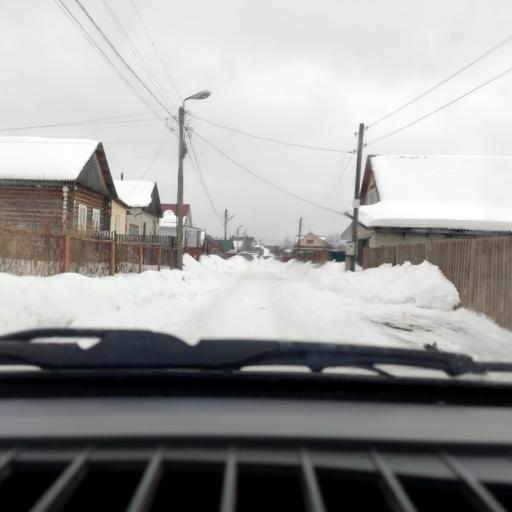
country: RU
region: Perm
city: Krasnokamsk
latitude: 58.0972
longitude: 55.8026
